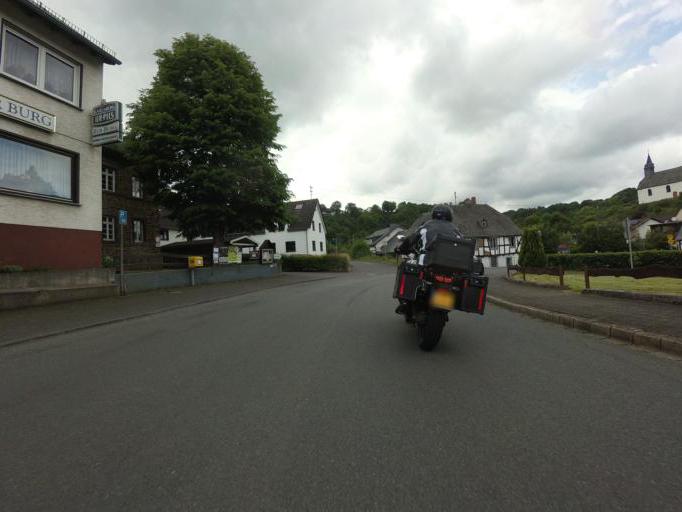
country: DE
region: Rheinland-Pfalz
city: Virneburg
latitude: 50.3418
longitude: 7.0786
